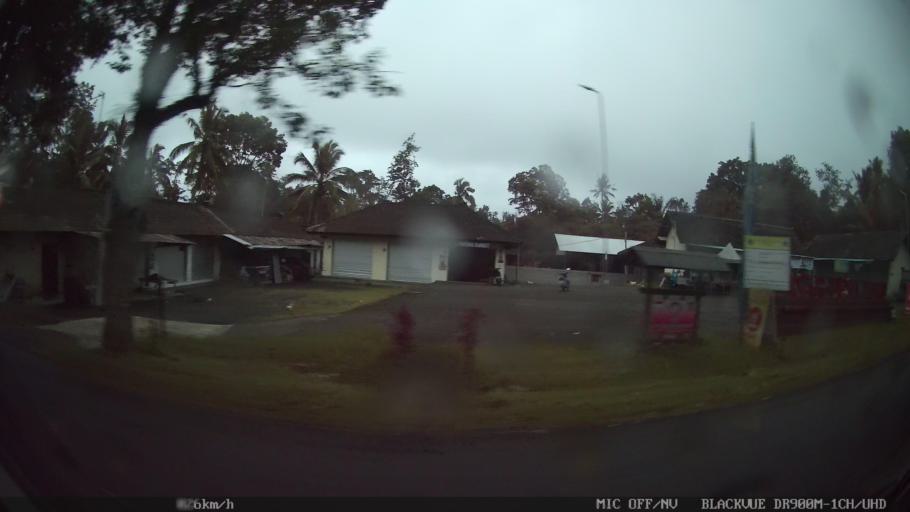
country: ID
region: Bali
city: Banjar Ponggang
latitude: -8.3863
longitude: 115.2623
